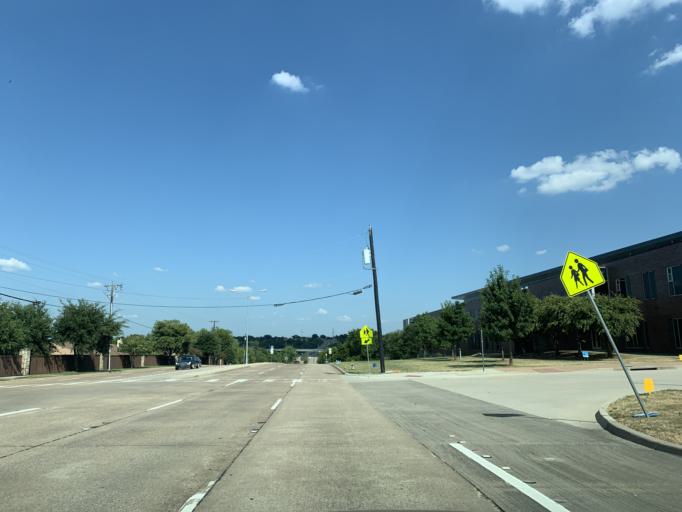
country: US
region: Texas
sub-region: Dallas County
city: Lancaster
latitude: 32.6632
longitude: -96.7955
